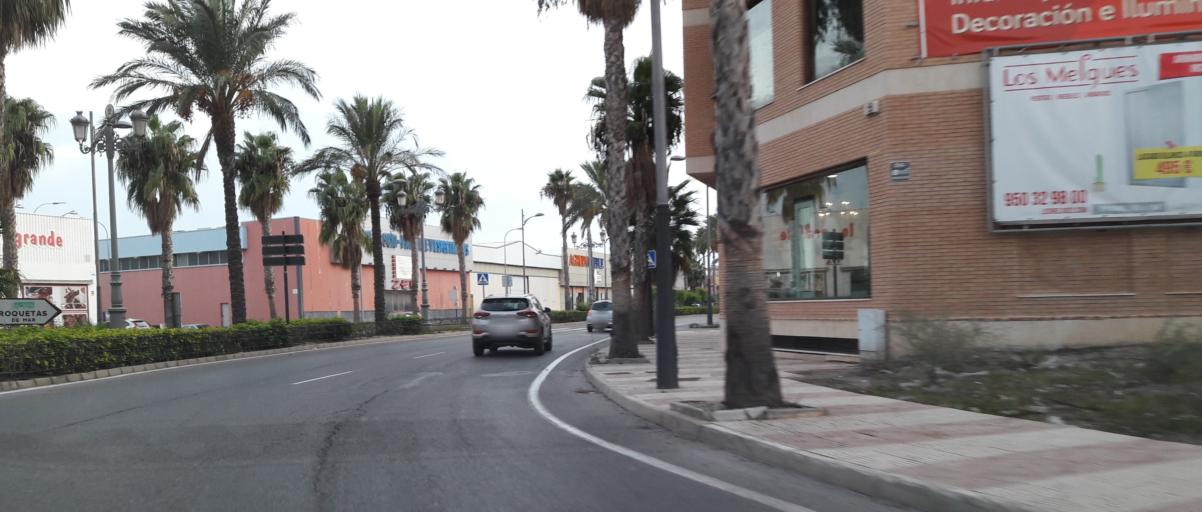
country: ES
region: Andalusia
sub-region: Provincia de Almeria
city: Roquetas de Mar
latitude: 36.7868
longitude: -2.6068
